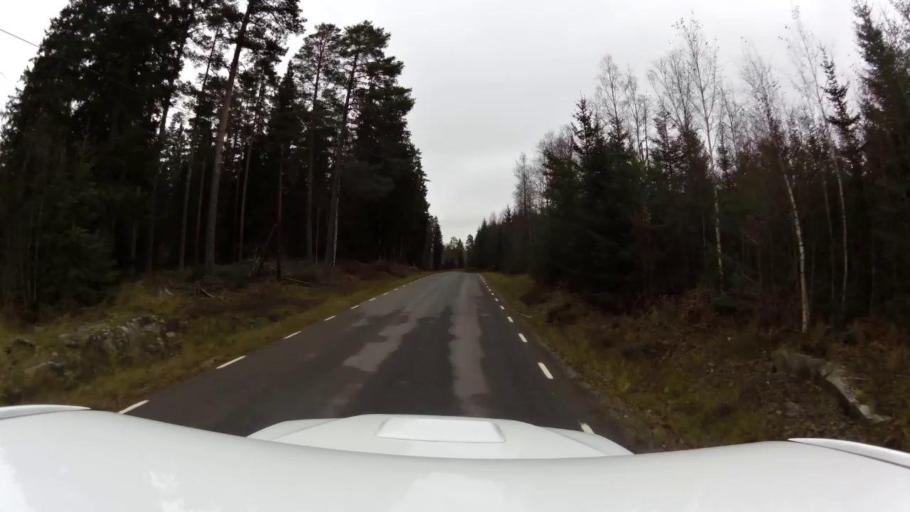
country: SE
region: OEstergoetland
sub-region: Kinda Kommun
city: Rimforsa
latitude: 58.1433
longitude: 15.4556
